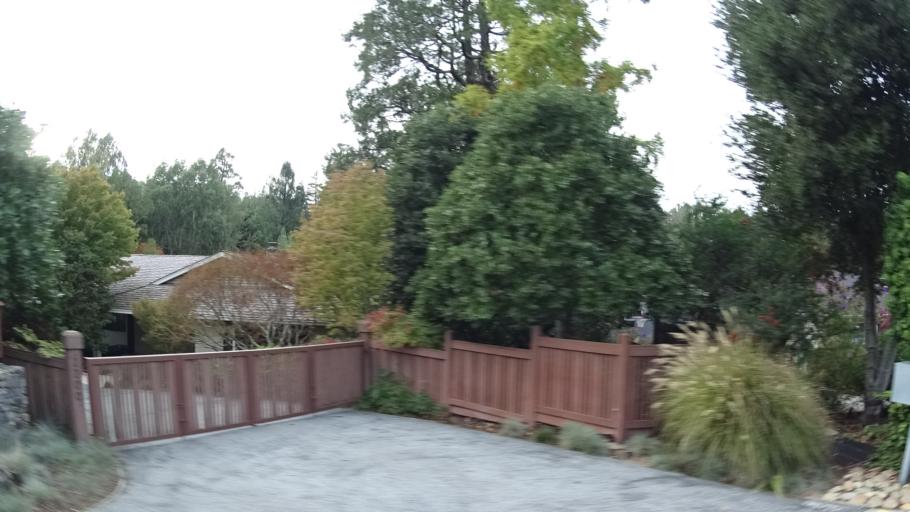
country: US
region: California
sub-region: San Mateo County
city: Hillsborough
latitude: 37.5715
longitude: -122.3687
